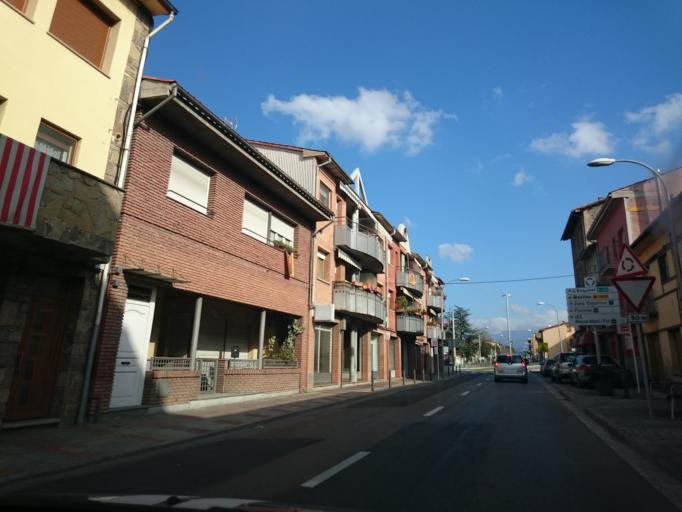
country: ES
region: Catalonia
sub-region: Provincia de Barcelona
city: Manlleu
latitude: 41.9853
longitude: 2.3106
